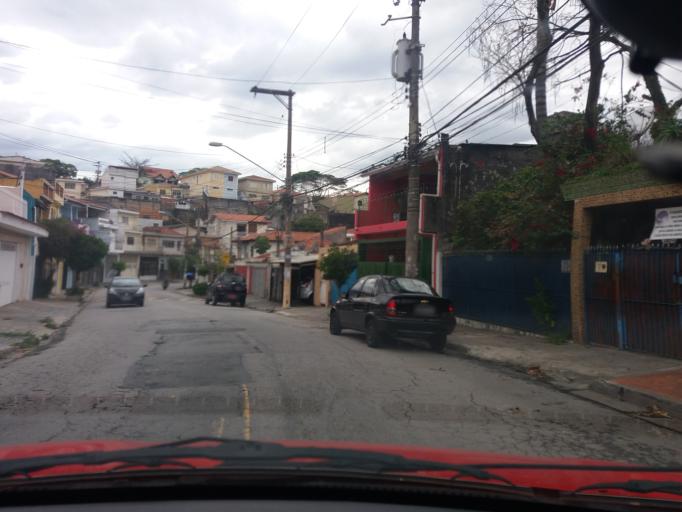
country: BR
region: Sao Paulo
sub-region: Taboao Da Serra
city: Taboao da Serra
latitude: -23.5834
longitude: -46.7391
